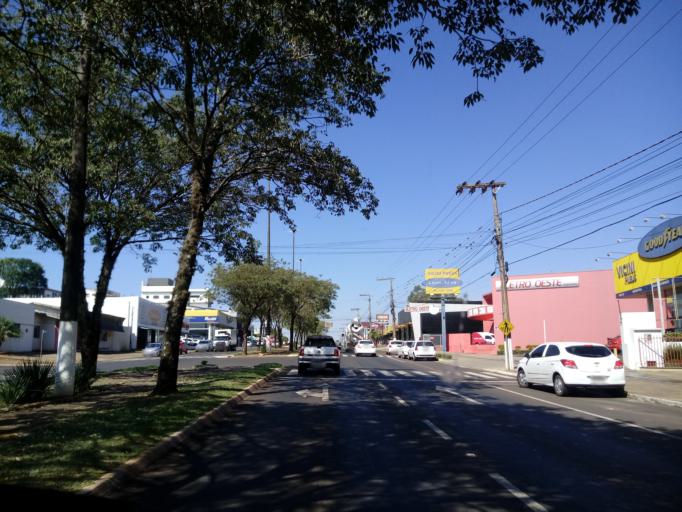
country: BR
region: Santa Catarina
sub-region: Chapeco
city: Chapeco
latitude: -27.0812
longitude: -52.6209
